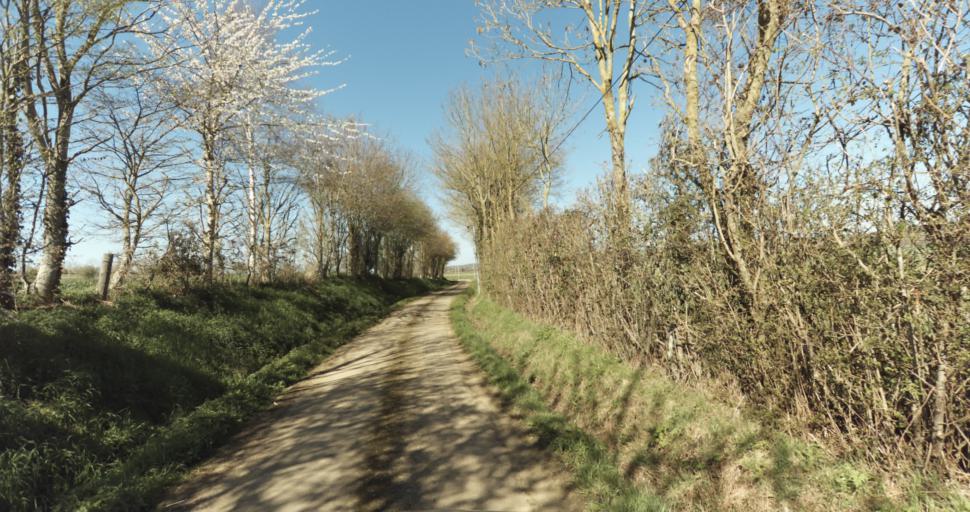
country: FR
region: Lower Normandy
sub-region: Departement du Calvados
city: Saint-Pierre-sur-Dives
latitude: 49.0202
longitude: 0.0142
